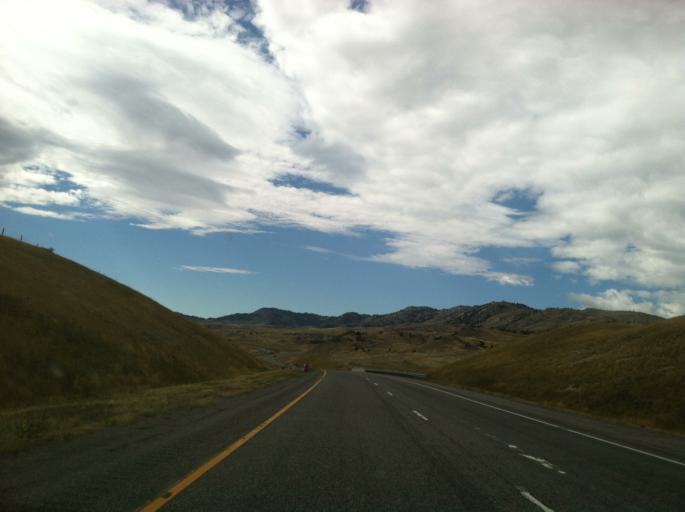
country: US
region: Montana
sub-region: Park County
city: Livingston
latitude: 45.6628
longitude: -110.6699
